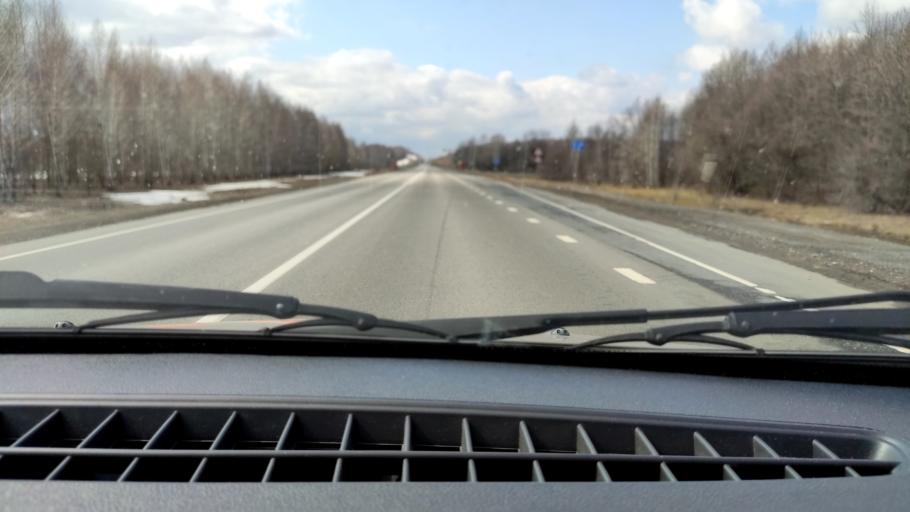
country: RU
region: Bashkortostan
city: Kudeyevskiy
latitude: 54.8002
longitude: 56.6050
